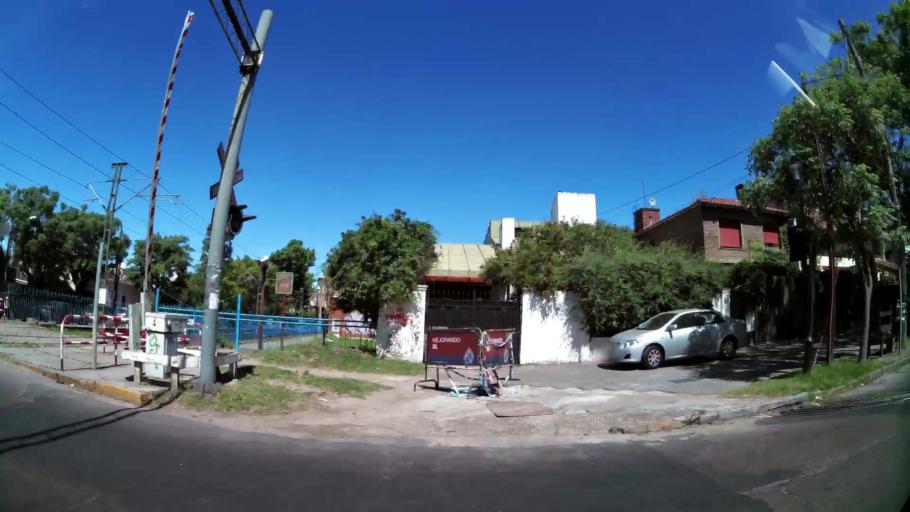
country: AR
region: Buenos Aires
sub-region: Partido de San Isidro
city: San Isidro
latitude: -34.4646
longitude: -58.5105
